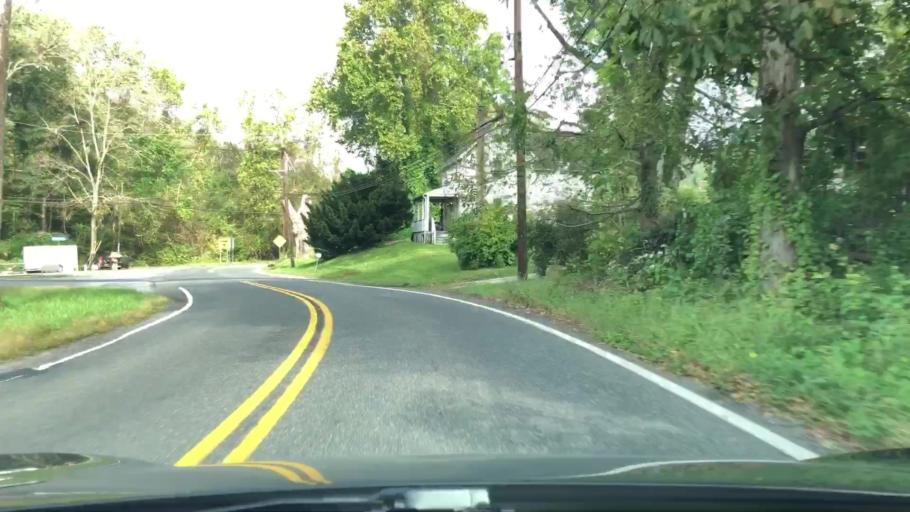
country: US
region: Pennsylvania
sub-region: Delaware County
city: Wayne
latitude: 40.0125
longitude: -75.3862
